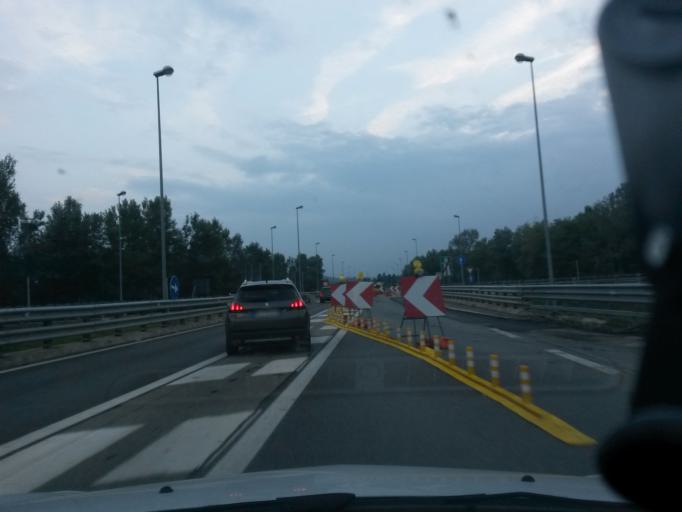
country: IT
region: Piedmont
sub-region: Provincia di Torino
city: Drubiaglio-Grangia
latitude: 45.0909
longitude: 7.4174
